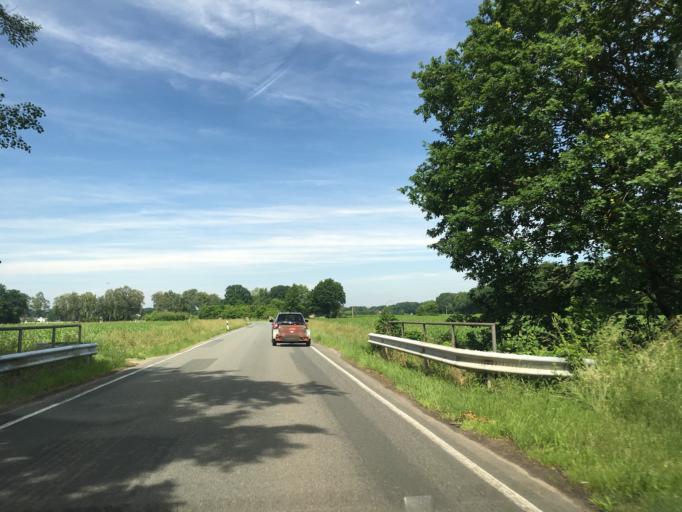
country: DE
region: North Rhine-Westphalia
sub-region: Regierungsbezirk Munster
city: Nordwalde
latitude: 52.1270
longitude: 7.4408
